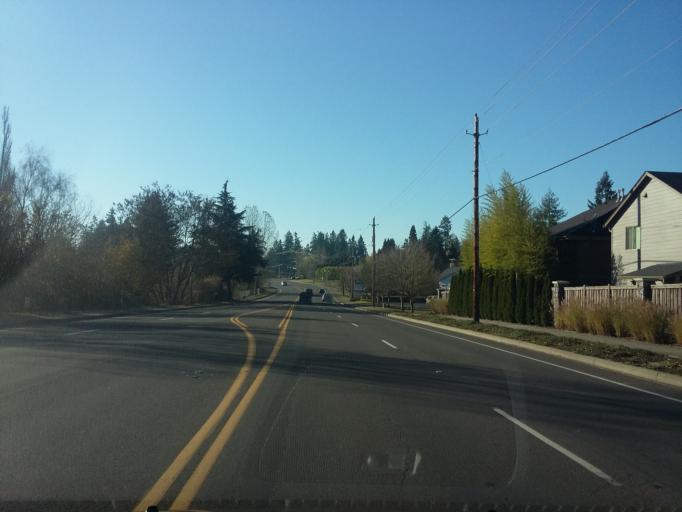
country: US
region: Washington
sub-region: Clark County
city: Barberton
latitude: 45.6881
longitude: -122.6227
